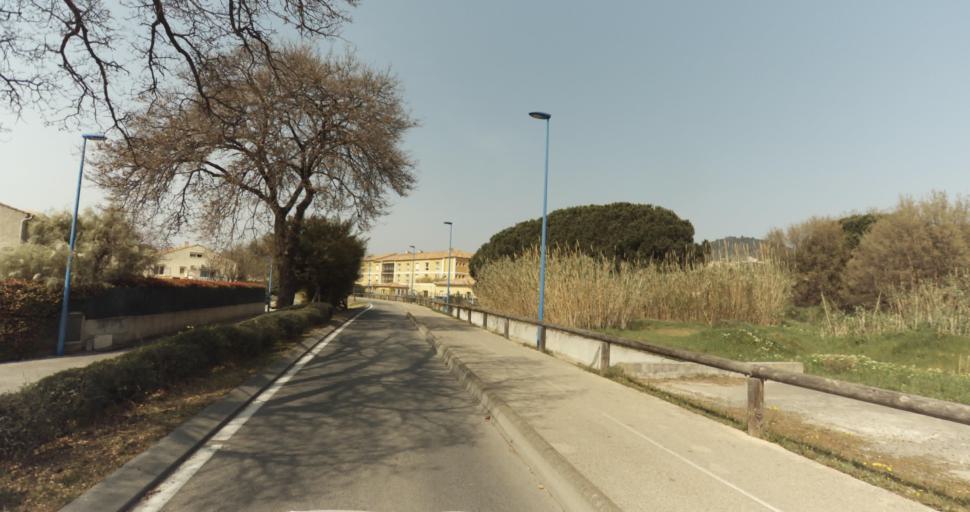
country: FR
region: Provence-Alpes-Cote d'Azur
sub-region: Departement du Var
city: Bormes-les-Mimosas
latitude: 43.1361
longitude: 6.3487
